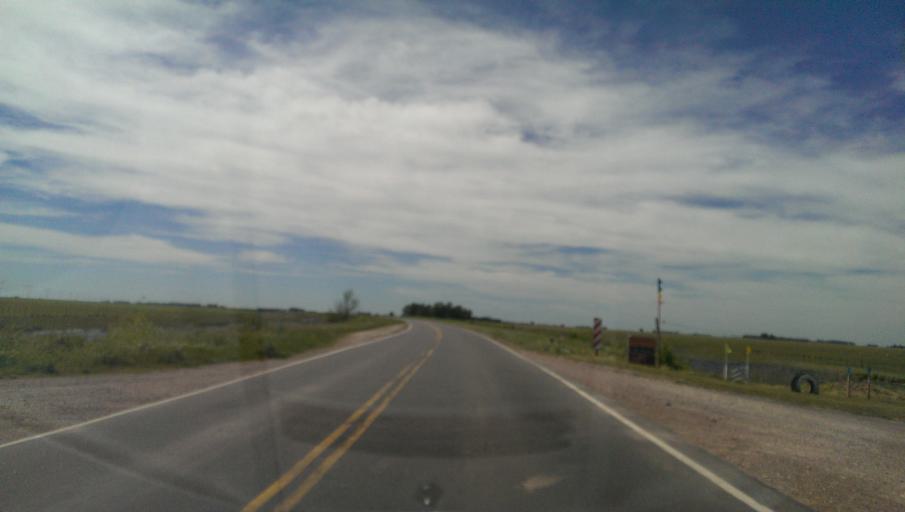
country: AR
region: Buenos Aires
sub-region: Partido de Laprida
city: Laprida
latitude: -37.2343
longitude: -60.7147
